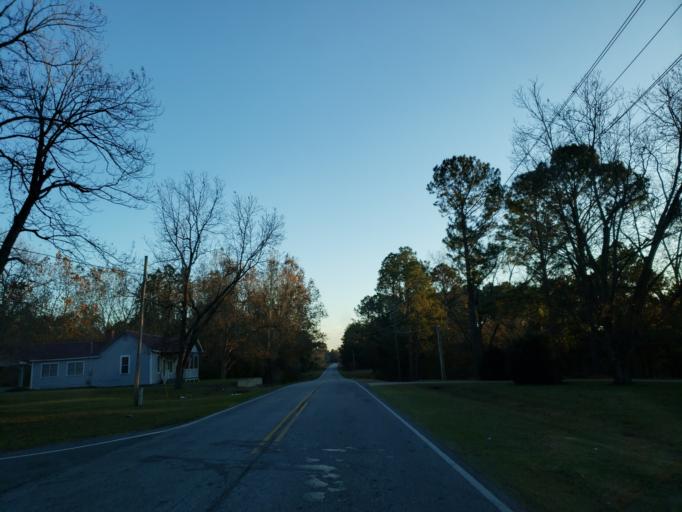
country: US
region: Georgia
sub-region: Crisp County
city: Cordele
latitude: 31.9353
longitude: -83.7662
